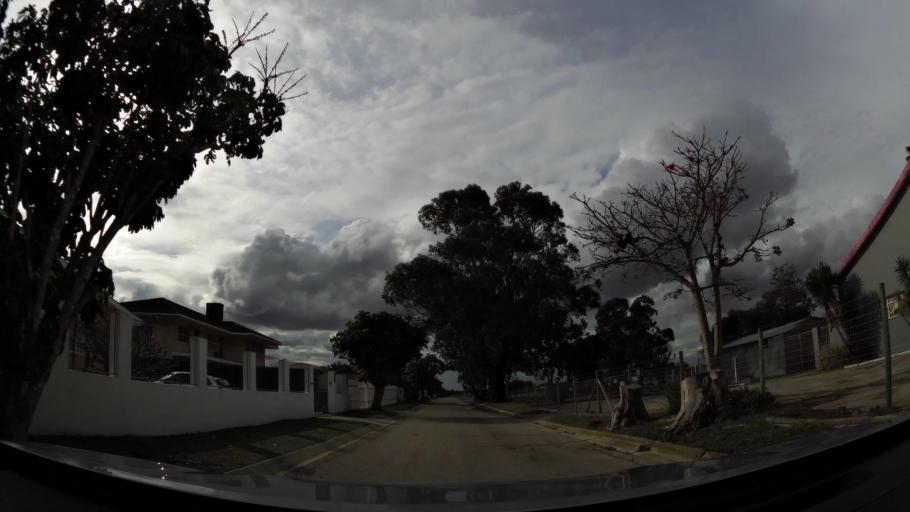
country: ZA
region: Eastern Cape
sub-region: Nelson Mandela Bay Metropolitan Municipality
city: Port Elizabeth
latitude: -33.9404
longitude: 25.5059
